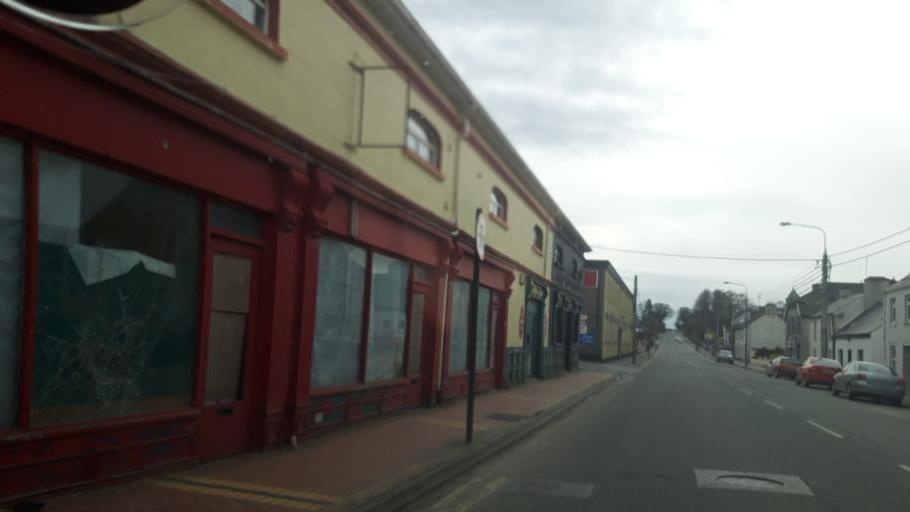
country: IE
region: Leinster
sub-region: Uibh Fhaili
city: Edenderry
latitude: 53.3401
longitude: -7.0571
